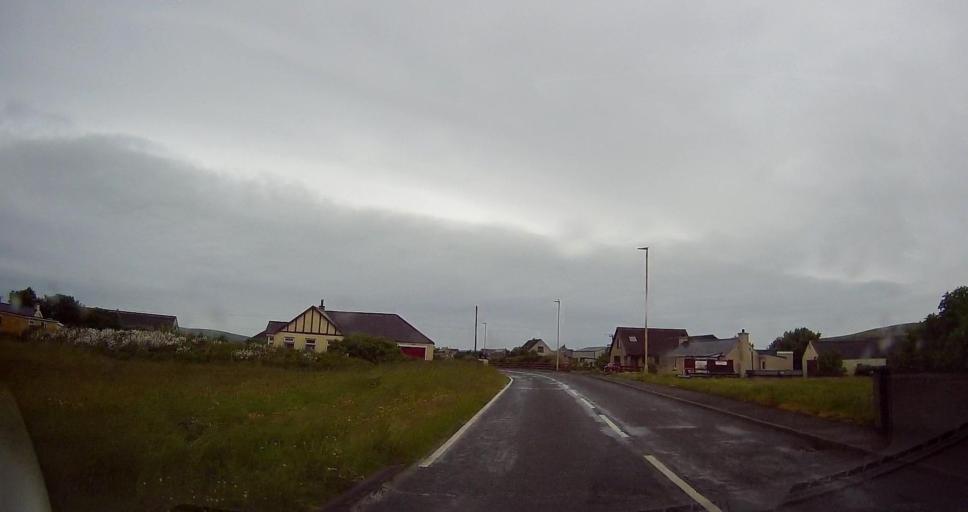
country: GB
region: Scotland
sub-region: Orkney Islands
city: Stromness
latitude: 59.0698
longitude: -3.2336
